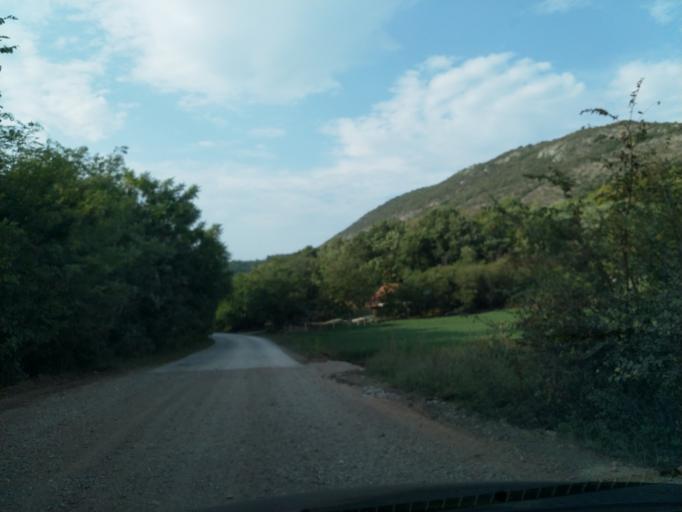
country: RS
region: Central Serbia
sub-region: Pomoravski Okrug
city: Paracin
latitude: 43.8361
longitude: 21.5404
